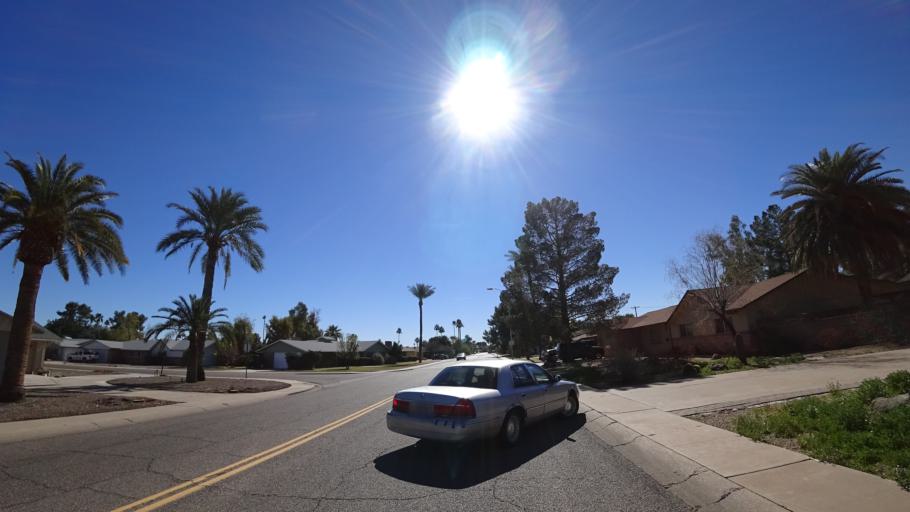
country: US
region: Arizona
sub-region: Maricopa County
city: Scottsdale
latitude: 33.5039
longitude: -111.8955
